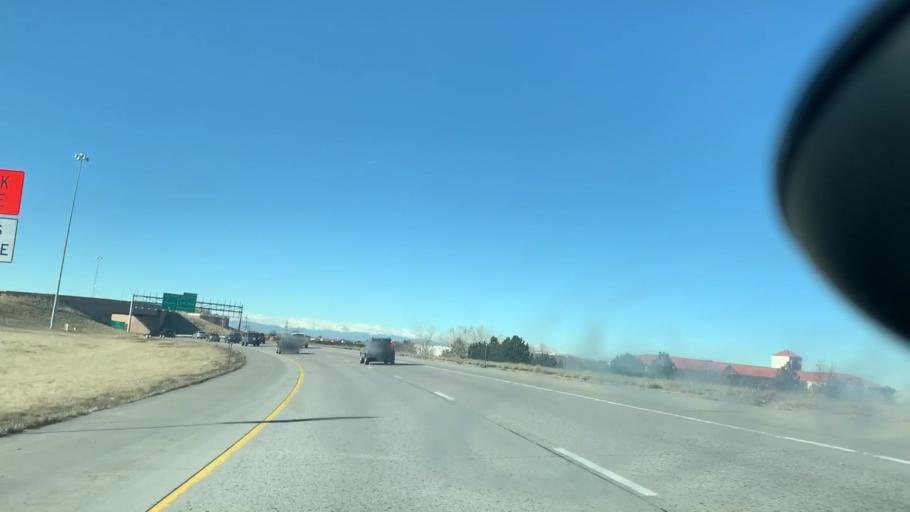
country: US
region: Colorado
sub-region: Adams County
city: Aurora
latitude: 39.7703
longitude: -104.8007
